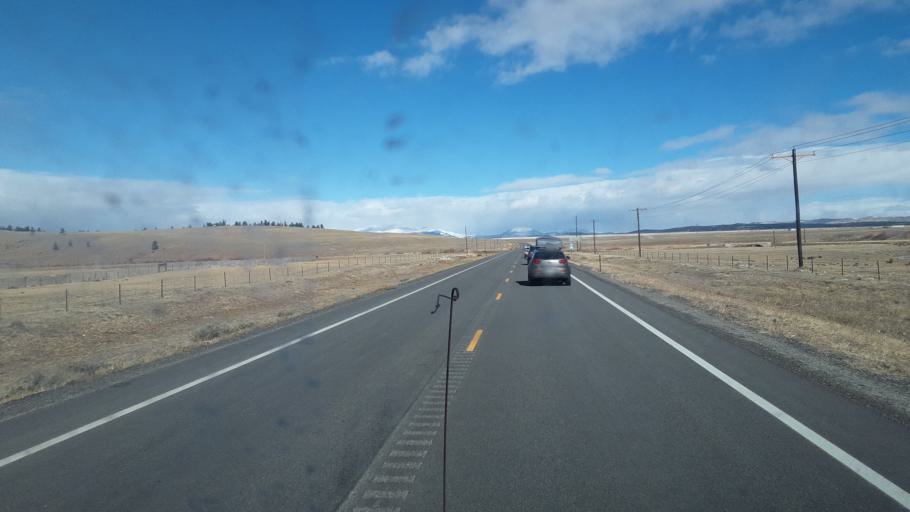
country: US
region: Colorado
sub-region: Park County
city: Fairplay
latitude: 39.0674
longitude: -105.9747
